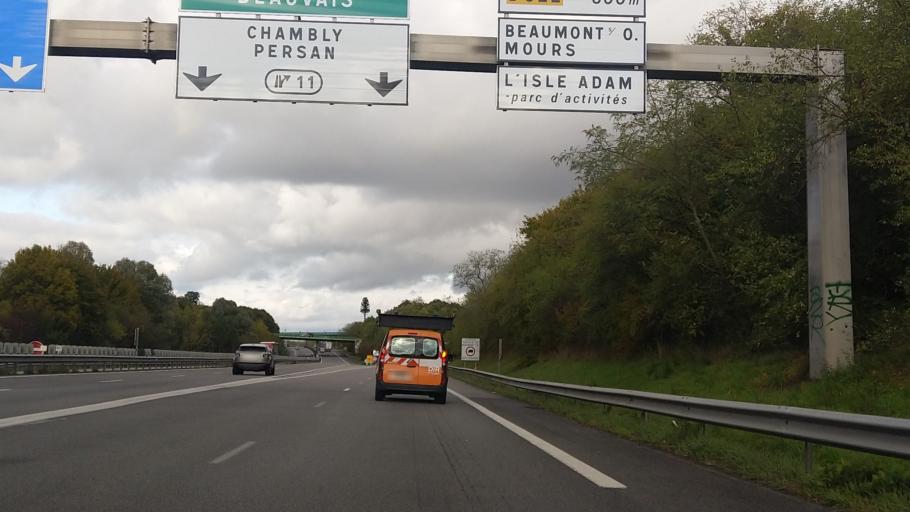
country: FR
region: Ile-de-France
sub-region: Departement du Val-d'Oise
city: Mours
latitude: 49.1197
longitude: 2.2540
